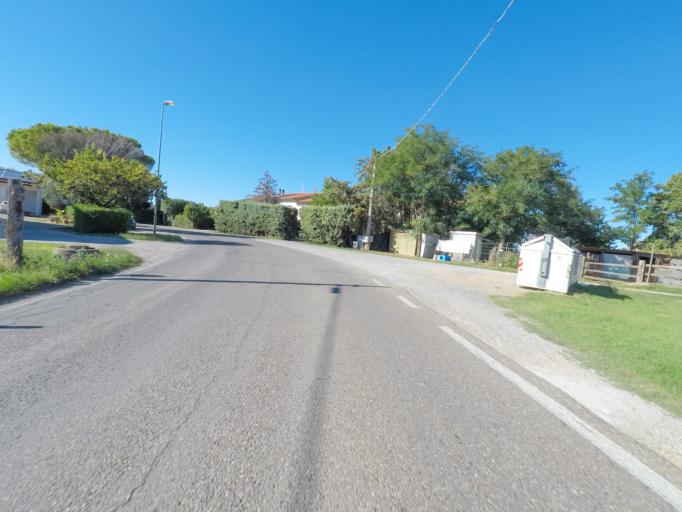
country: IT
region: Tuscany
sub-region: Provincia di Grosseto
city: Grosseto
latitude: 42.7697
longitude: 11.1416
